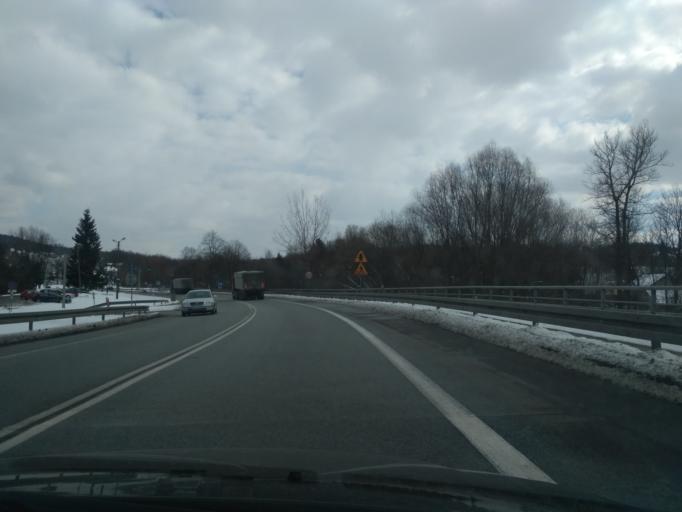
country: PL
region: Subcarpathian Voivodeship
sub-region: Powiat strzyzowski
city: Babica
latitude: 49.9292
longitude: 21.8729
